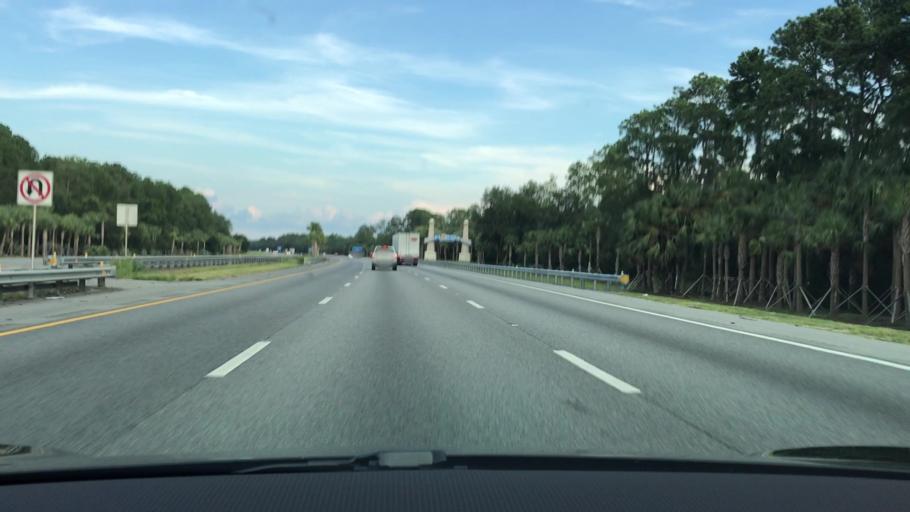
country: US
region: Georgia
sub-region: Echols County
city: Statenville
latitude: 30.6252
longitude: -83.1714
